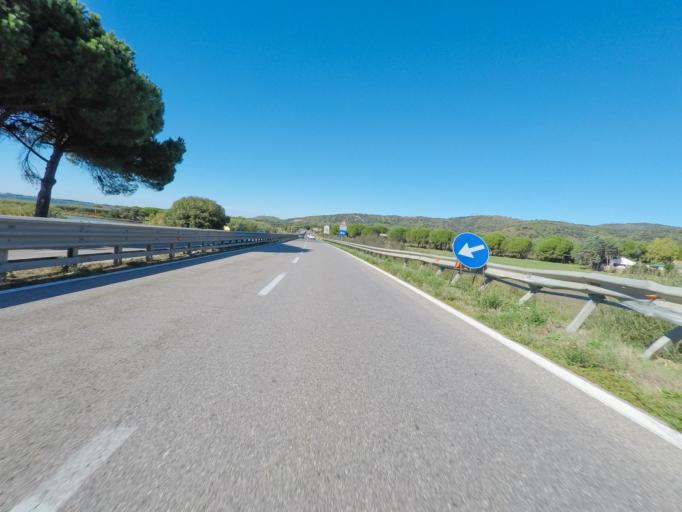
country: IT
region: Tuscany
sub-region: Provincia di Grosseto
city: Orbetello Scalo
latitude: 42.4307
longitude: 11.2849
